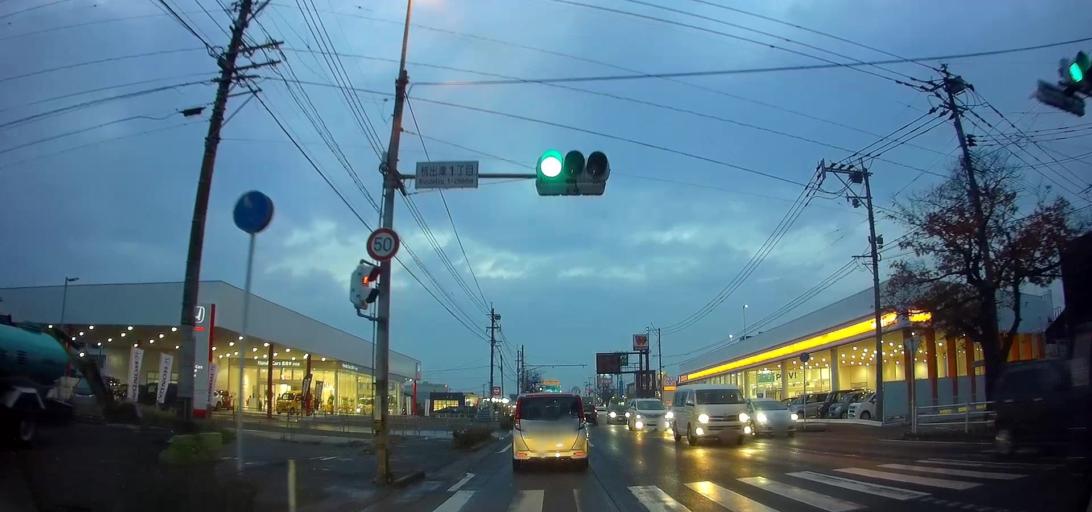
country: JP
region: Nagasaki
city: Omura
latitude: 32.9100
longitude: 129.9533
